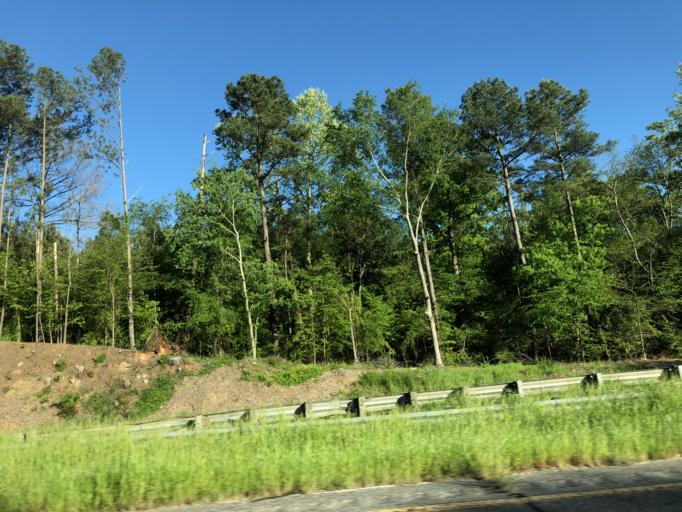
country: US
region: Georgia
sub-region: Clarke County
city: Country Club Estates
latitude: 33.9566
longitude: -83.4367
